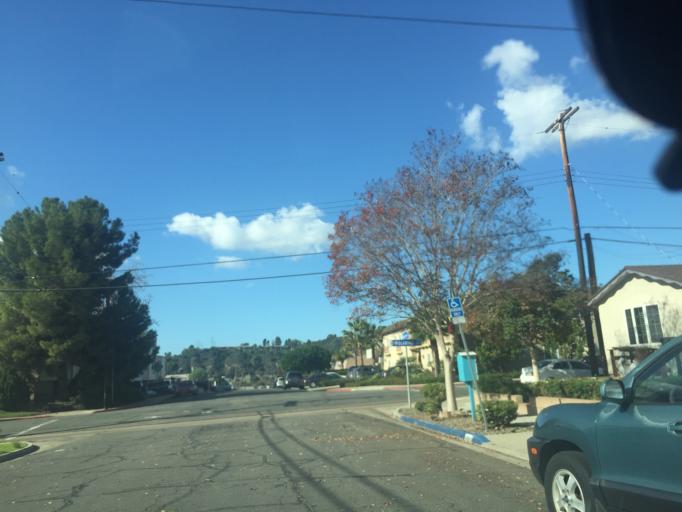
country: US
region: California
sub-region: San Diego County
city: La Mesa
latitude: 32.7887
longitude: -117.0955
